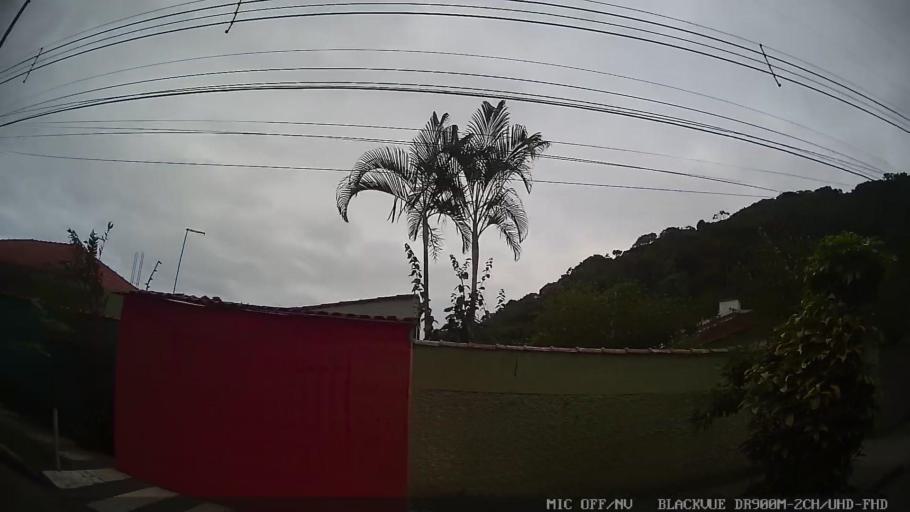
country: BR
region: Sao Paulo
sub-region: Guaruja
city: Guaruja
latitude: -23.9888
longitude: -46.2544
